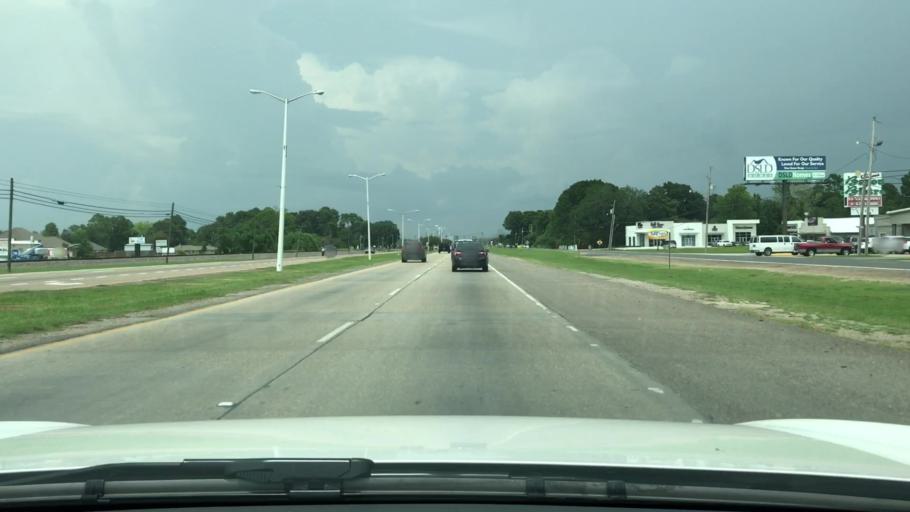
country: US
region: Louisiana
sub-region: West Baton Rouge Parish
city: Brusly
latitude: 30.3867
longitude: -91.2447
